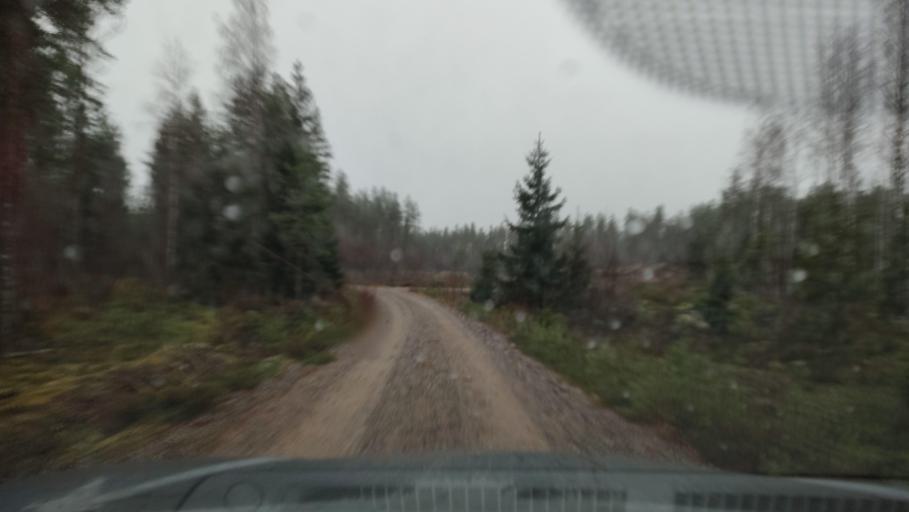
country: FI
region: Southern Ostrobothnia
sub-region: Suupohja
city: Karijoki
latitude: 62.1876
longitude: 21.7380
